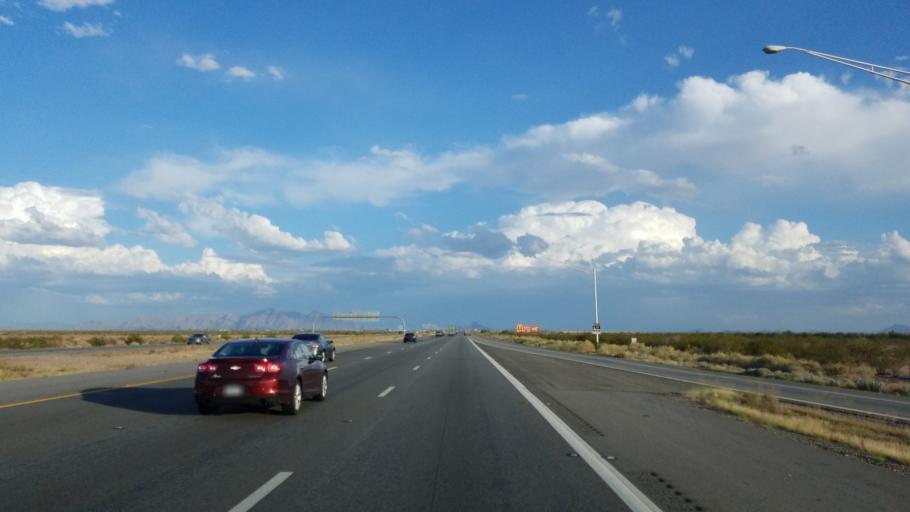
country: US
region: Arizona
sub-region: Pinal County
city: Arizona City
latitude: 32.8069
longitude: -111.6676
